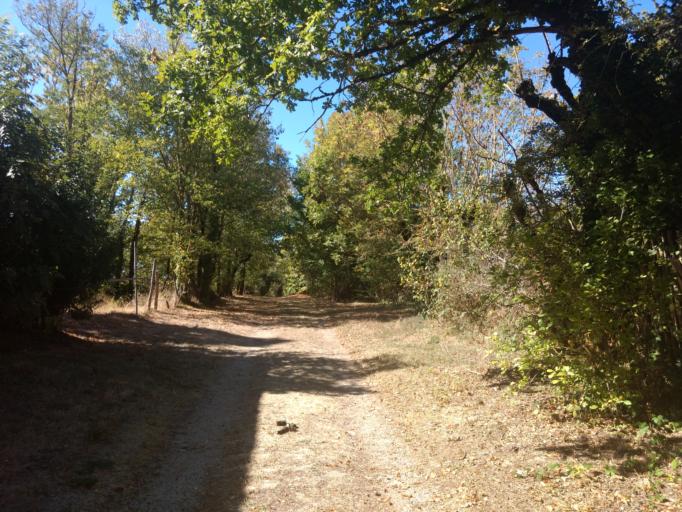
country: FR
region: Midi-Pyrenees
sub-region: Departement de l'Aveyron
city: Olemps
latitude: 44.3580
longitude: 2.5546
